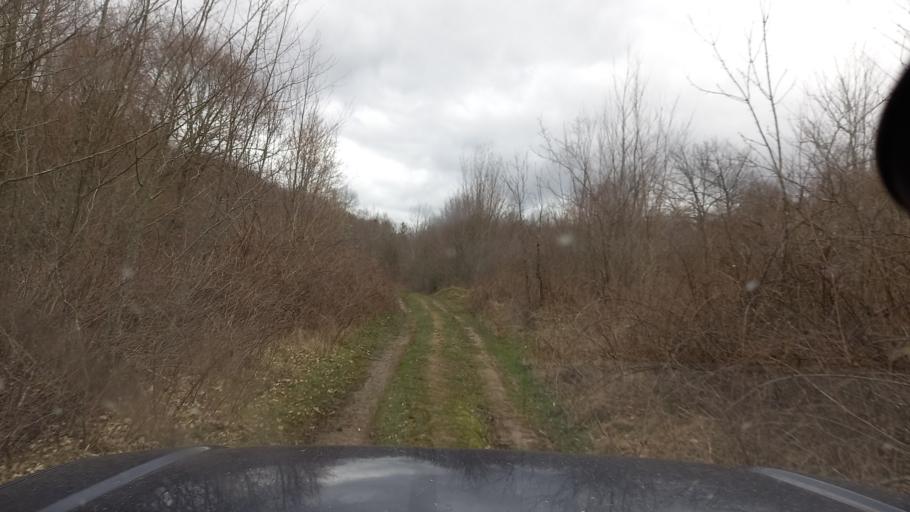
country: RU
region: Krasnodarskiy
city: Pshada
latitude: 44.4880
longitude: 38.3957
